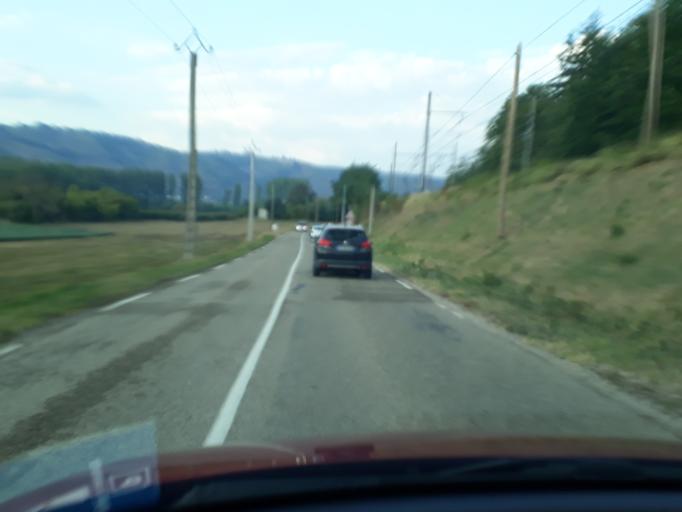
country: FR
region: Rhone-Alpes
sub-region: Departement du Rhone
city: Condrieu
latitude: 45.4676
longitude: 4.7906
